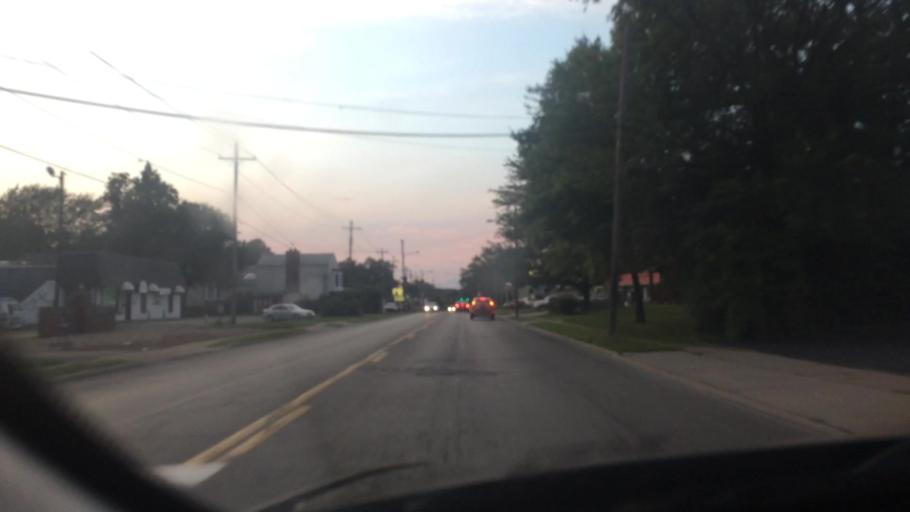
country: US
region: Michigan
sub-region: Monroe County
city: Lambertville
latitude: 41.7149
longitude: -83.6142
